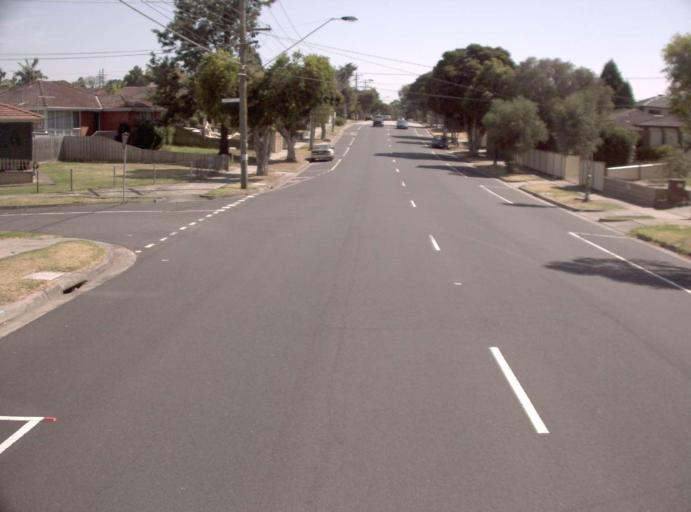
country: AU
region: Victoria
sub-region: Greater Dandenong
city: Noble Park North
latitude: -37.9535
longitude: 145.1910
